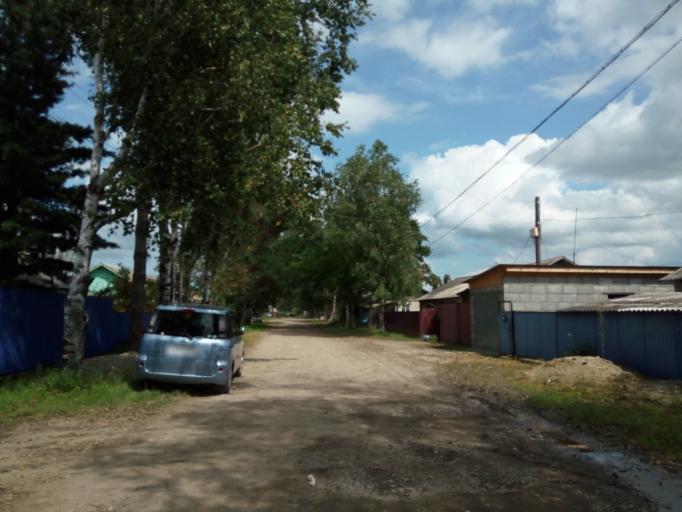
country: RU
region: Primorskiy
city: Dal'nerechensk
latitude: 45.9520
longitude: 133.8087
